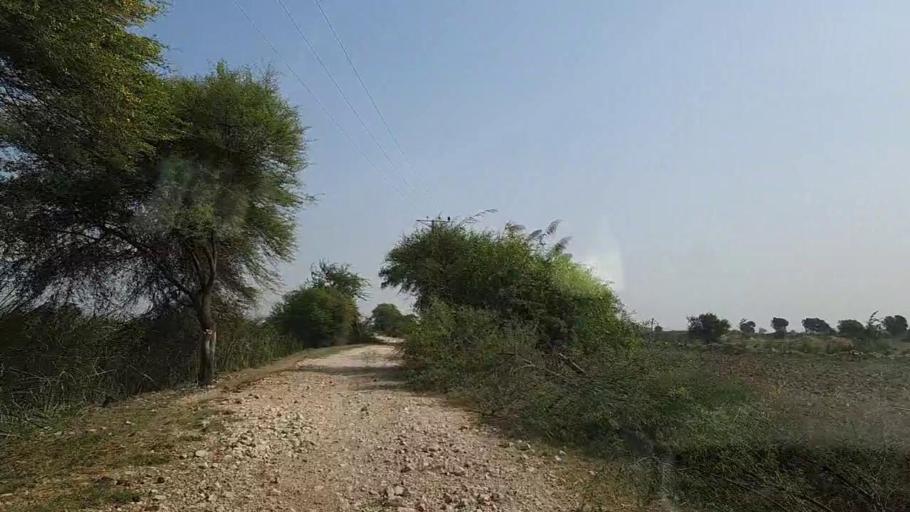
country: PK
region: Sindh
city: Mirpur Sakro
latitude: 24.5277
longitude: 67.8017
